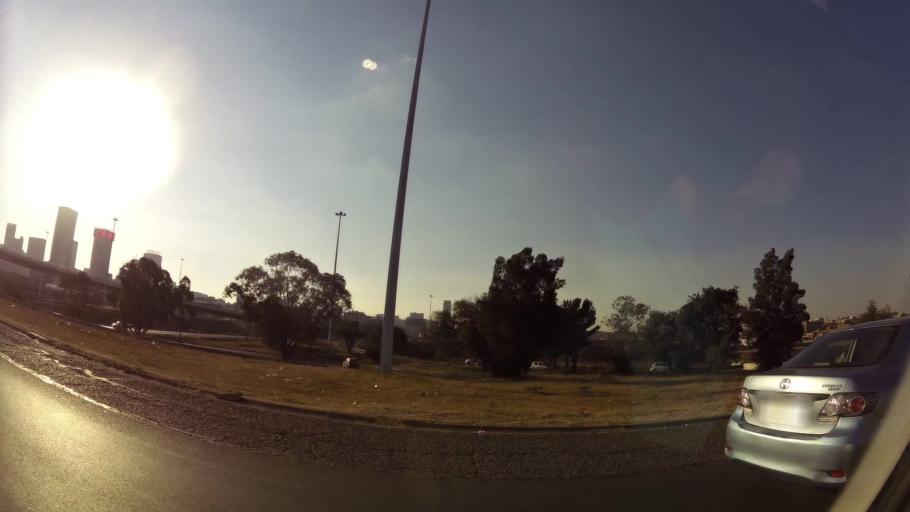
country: ZA
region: Gauteng
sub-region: City of Johannesburg Metropolitan Municipality
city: Johannesburg
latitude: -26.2126
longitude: 28.0572
